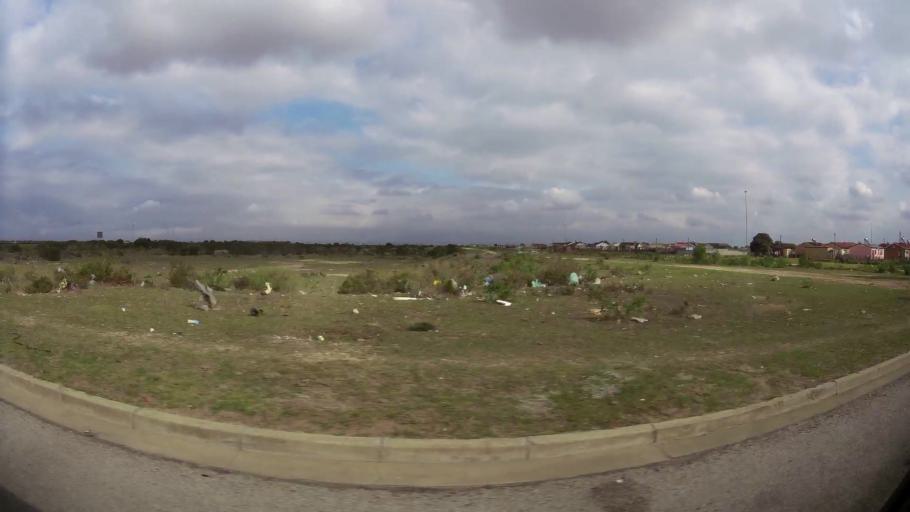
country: ZA
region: Eastern Cape
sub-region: Nelson Mandela Bay Metropolitan Municipality
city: Port Elizabeth
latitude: -33.8112
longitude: 25.6140
